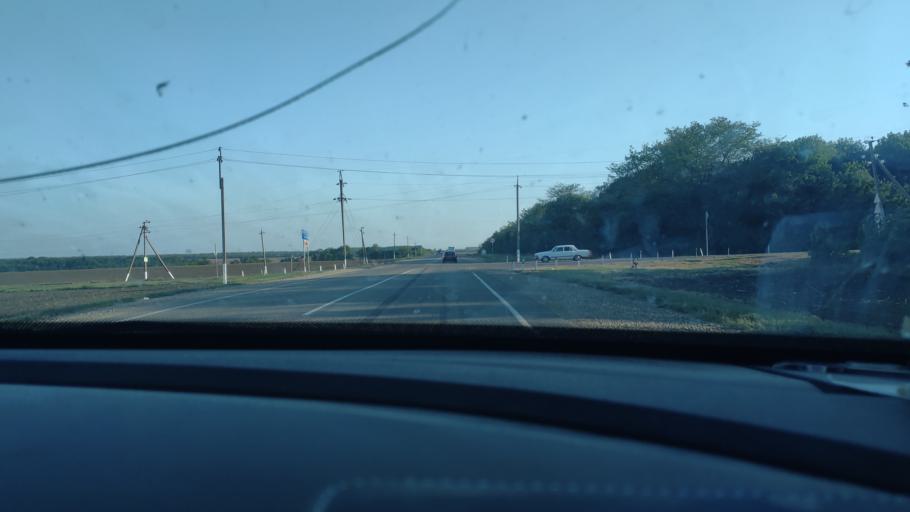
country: RU
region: Krasnodarskiy
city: Novominskaya
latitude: 46.2992
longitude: 38.9328
